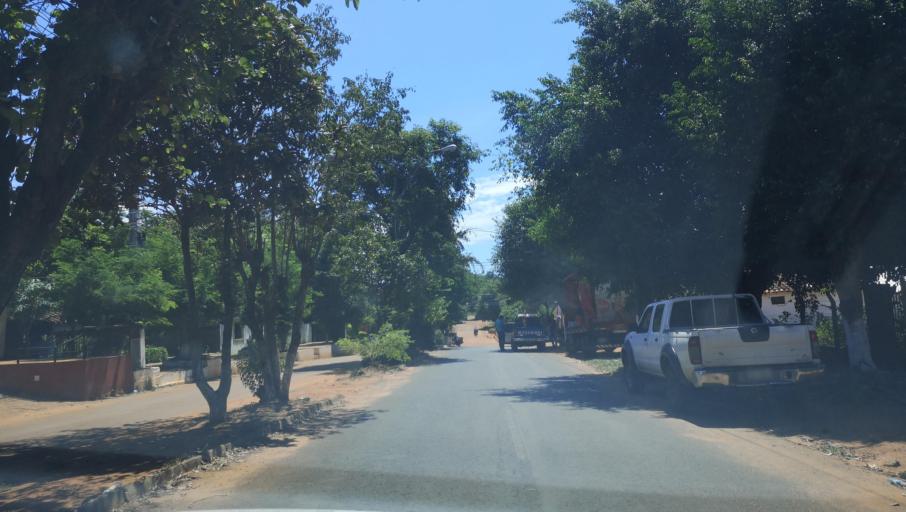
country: PY
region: Misiones
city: Santa Maria
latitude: -26.8844
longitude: -57.0299
